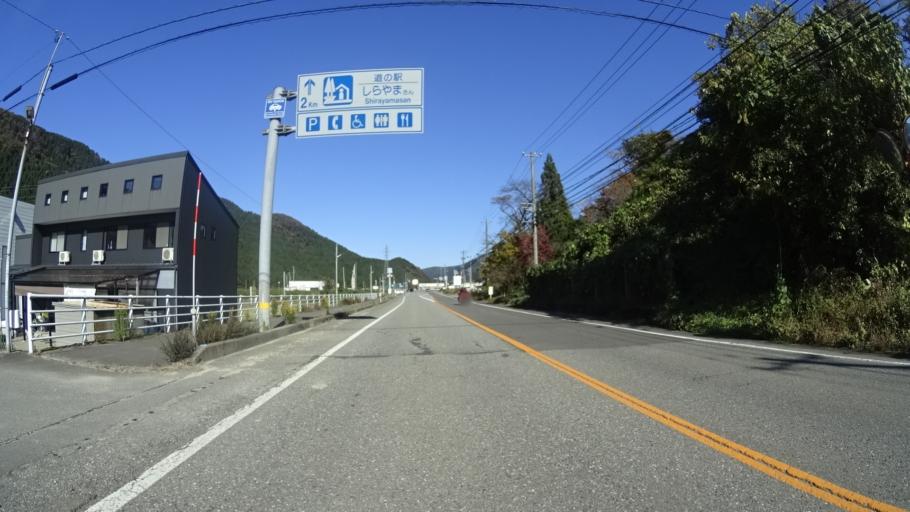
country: JP
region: Ishikawa
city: Tsurugi-asahimachi
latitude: 36.4211
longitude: 136.6312
